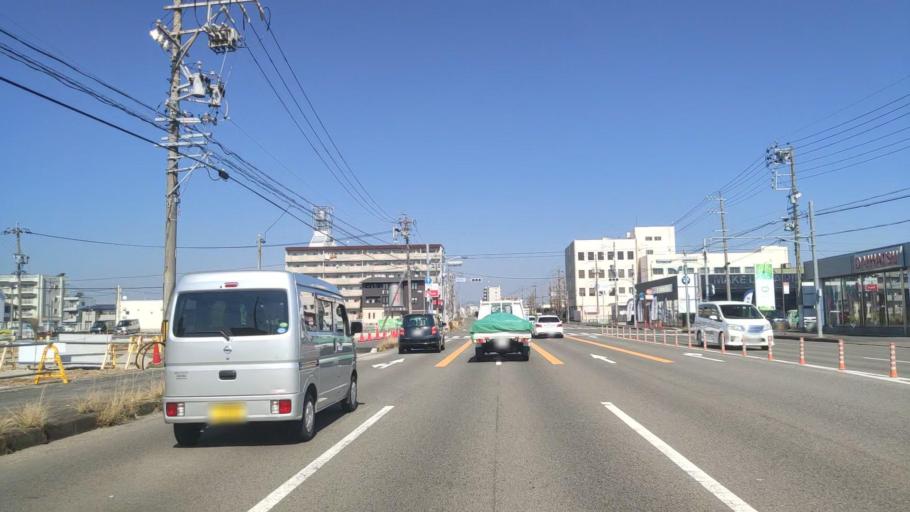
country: JP
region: Gifu
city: Kasamatsucho
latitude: 35.3916
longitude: 136.7476
